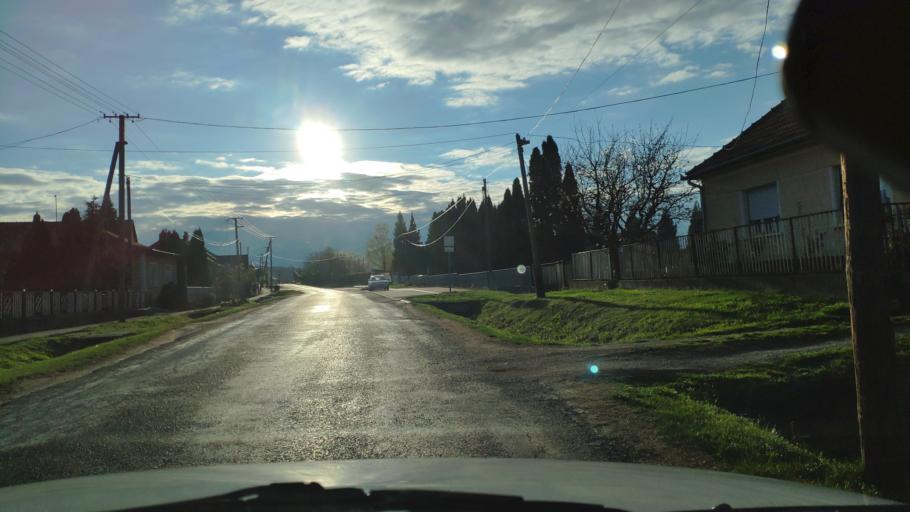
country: HU
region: Zala
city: Zalakomar
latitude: 46.4228
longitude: 17.1296
